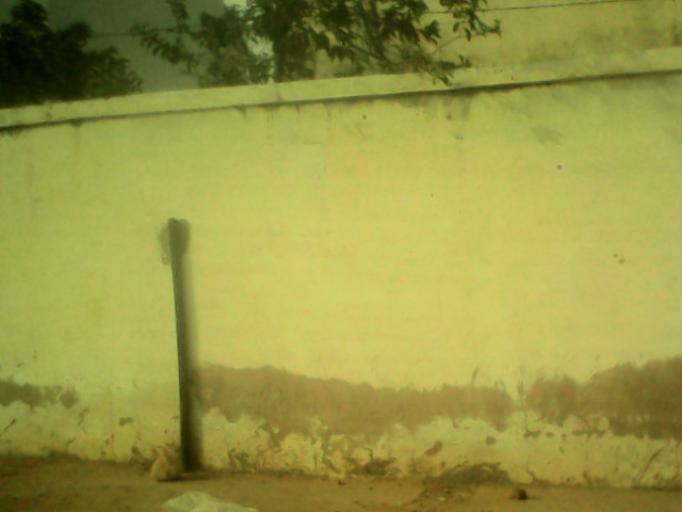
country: SN
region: Diourbel
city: Touba
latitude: 14.8620
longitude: -15.8680
